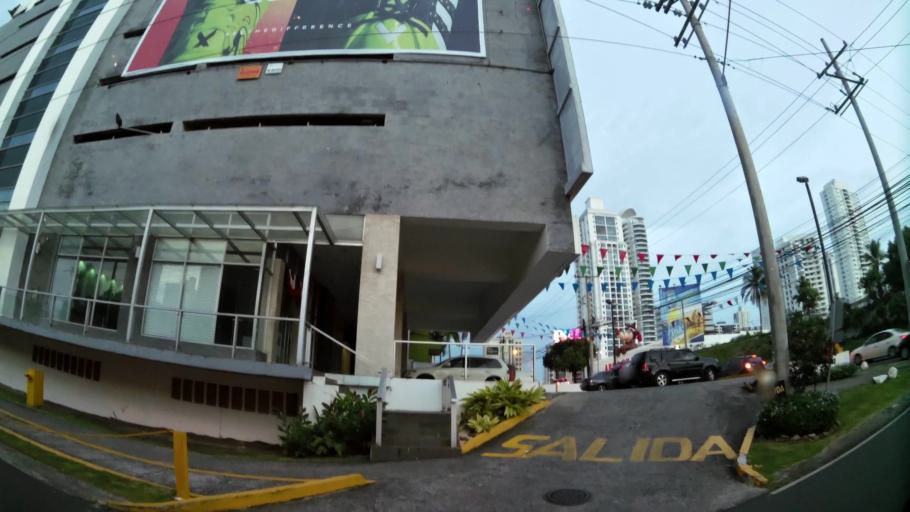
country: PA
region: Panama
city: Panama
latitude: 8.9925
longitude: -79.5085
